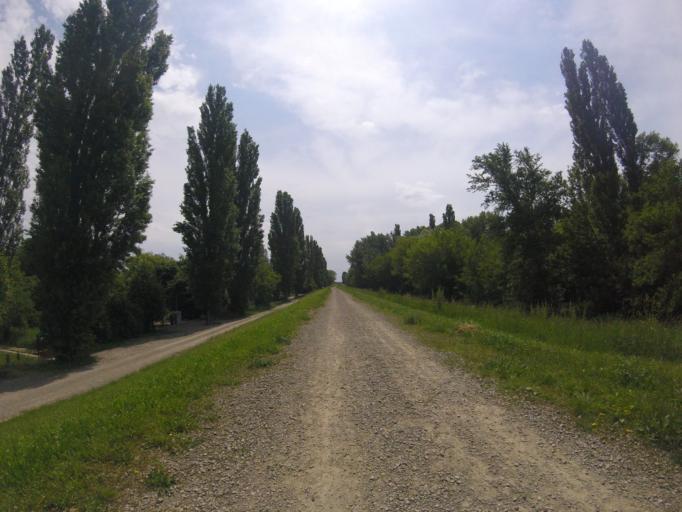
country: HU
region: Pest
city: Tahitotfalu
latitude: 47.7487
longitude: 19.0891
